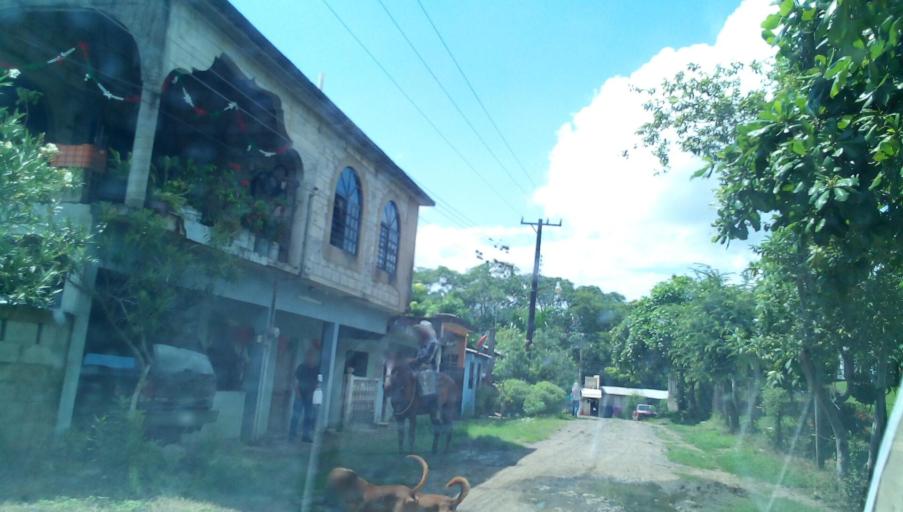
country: MX
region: Veracruz
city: Tamalin
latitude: 21.3682
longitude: -97.7987
